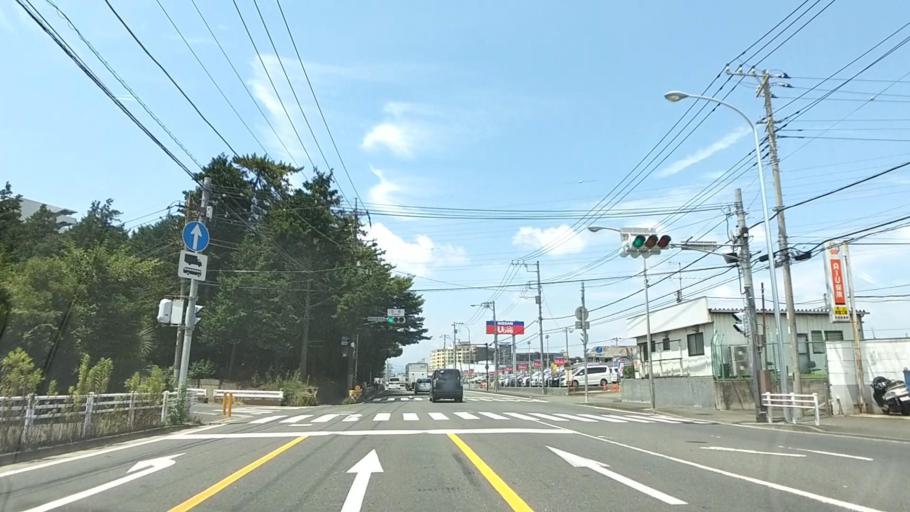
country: JP
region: Kanagawa
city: Minami-rinkan
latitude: 35.4982
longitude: 139.4774
